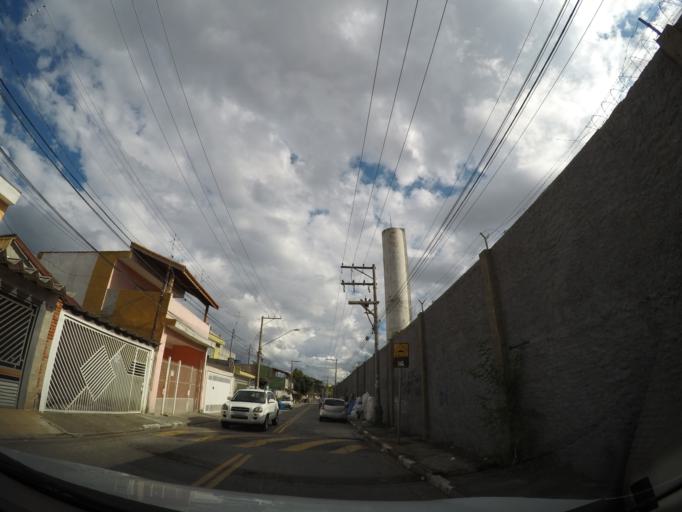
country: BR
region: Sao Paulo
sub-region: Guarulhos
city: Guarulhos
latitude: -23.4737
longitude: -46.5533
